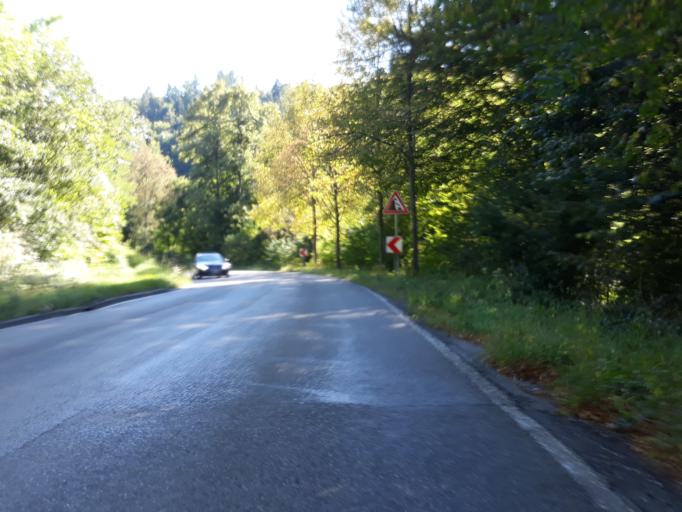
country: DE
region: Baden-Wuerttemberg
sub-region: Regierungsbezirk Stuttgart
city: Aidlingen
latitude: 48.6690
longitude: 8.9140
